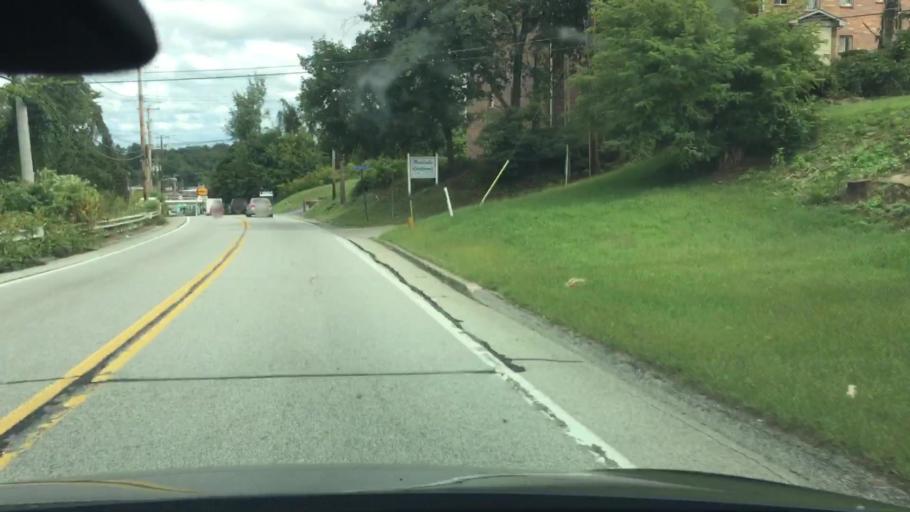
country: US
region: Pennsylvania
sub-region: Allegheny County
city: Penn Hills
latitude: 40.4819
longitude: -79.8210
